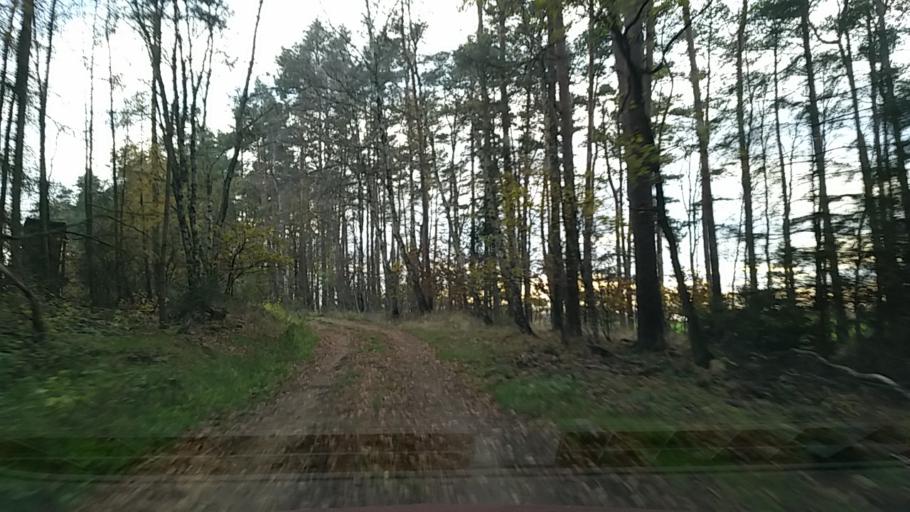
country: DE
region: Lower Saxony
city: Sprakensehl
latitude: 52.7960
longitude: 10.5104
